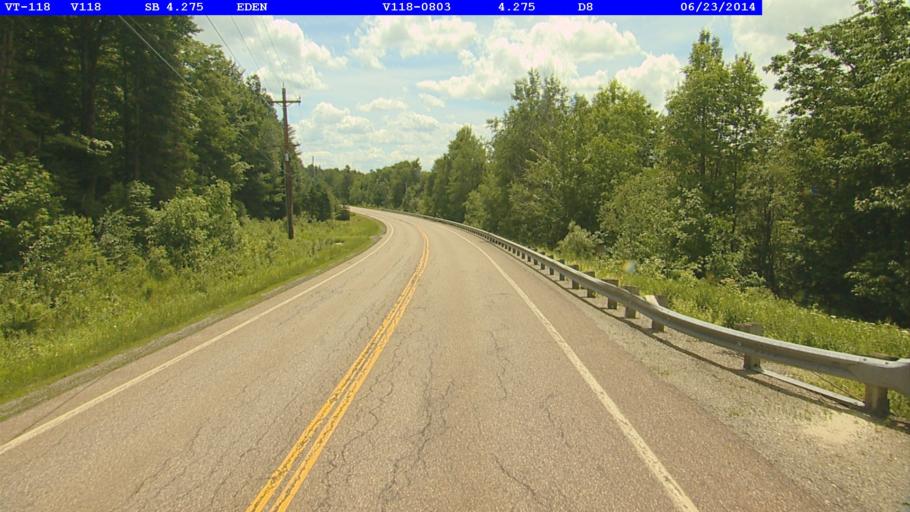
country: US
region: Vermont
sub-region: Lamoille County
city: Johnson
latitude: 44.7600
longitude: -72.5841
